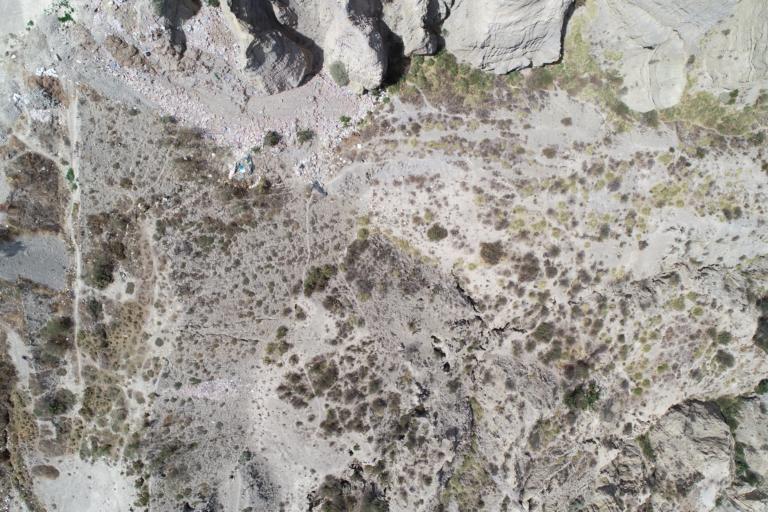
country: BO
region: La Paz
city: La Paz
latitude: -16.5216
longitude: -68.0757
